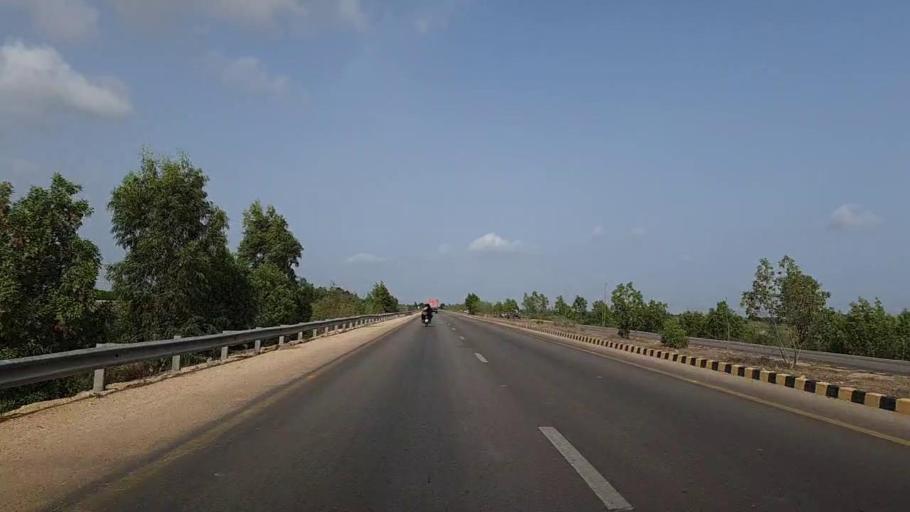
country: PK
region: Sindh
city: Gharo
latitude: 24.7314
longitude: 67.6550
